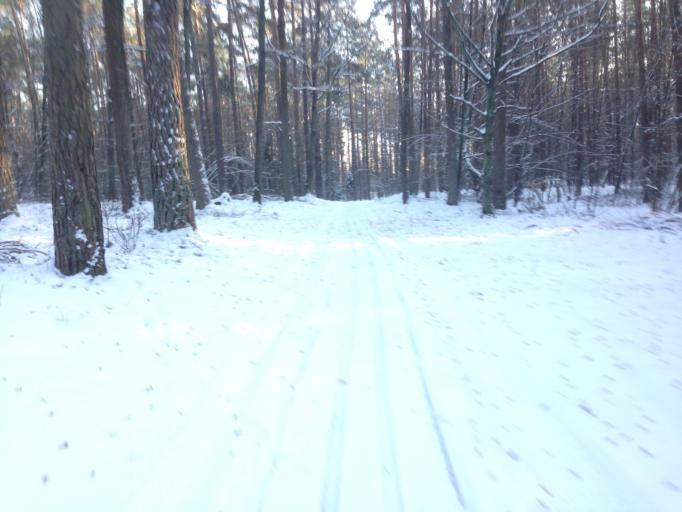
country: PL
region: Kujawsko-Pomorskie
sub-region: Powiat brodnicki
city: Gorzno
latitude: 53.1899
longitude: 19.6801
